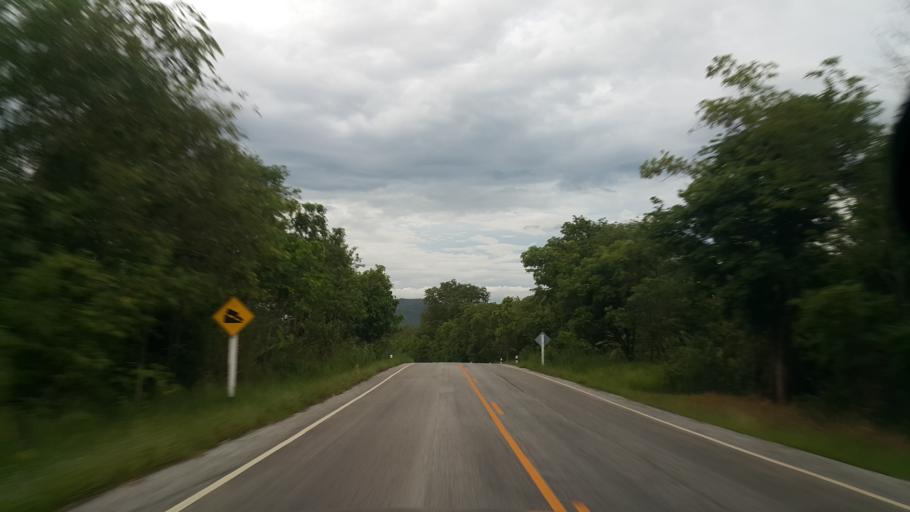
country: TH
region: Loei
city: Na Haeo
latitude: 17.4876
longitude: 101.1759
